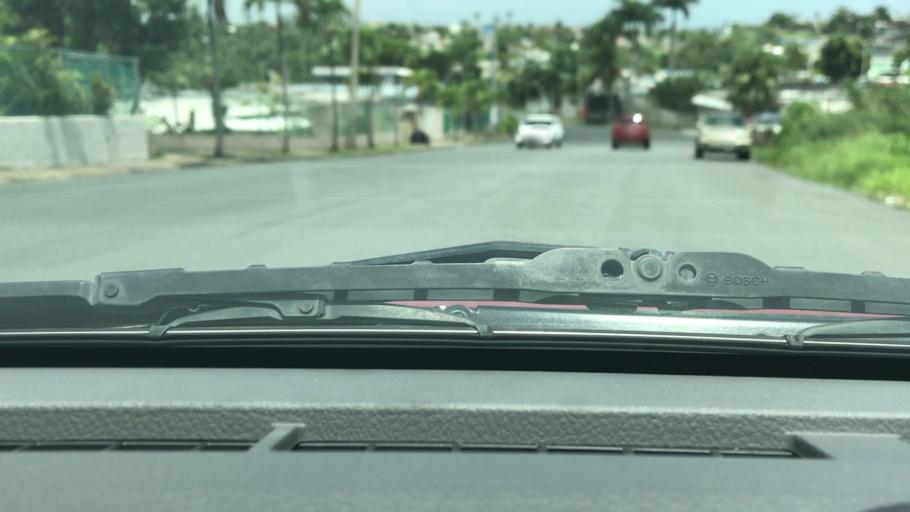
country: PR
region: Toa Alta
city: Pajaros
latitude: 18.3552
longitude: -66.1905
